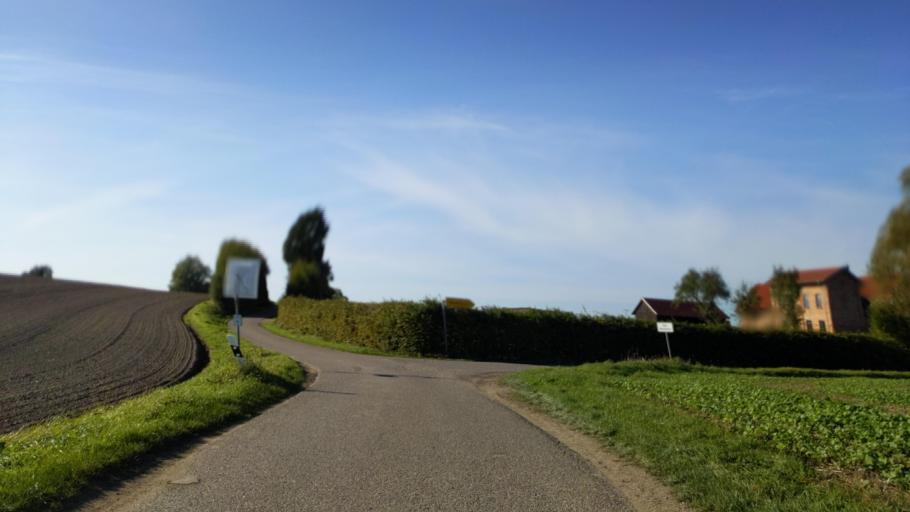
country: DE
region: Schleswig-Holstein
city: Ahrensbok
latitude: 54.0531
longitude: 10.5931
